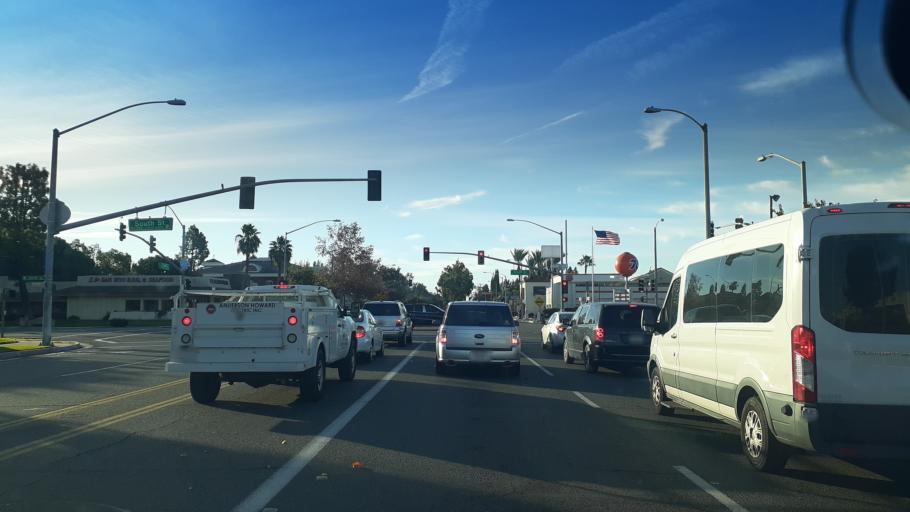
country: US
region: California
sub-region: Los Angeles County
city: Artesia
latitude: 33.8589
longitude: -118.0822
